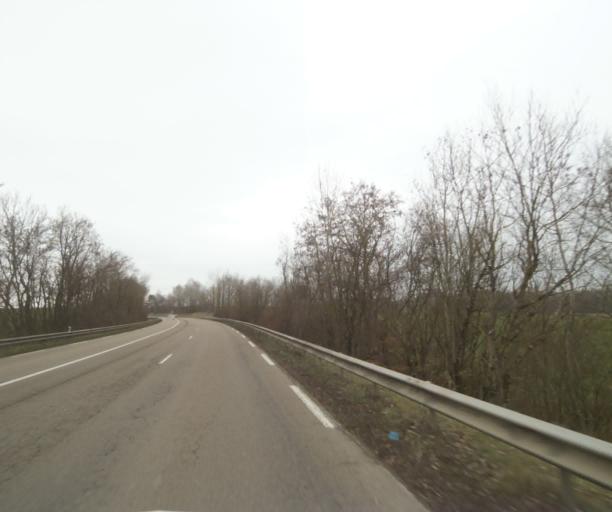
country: FR
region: Champagne-Ardenne
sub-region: Departement de la Haute-Marne
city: Bienville
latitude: 48.5863
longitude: 5.0287
